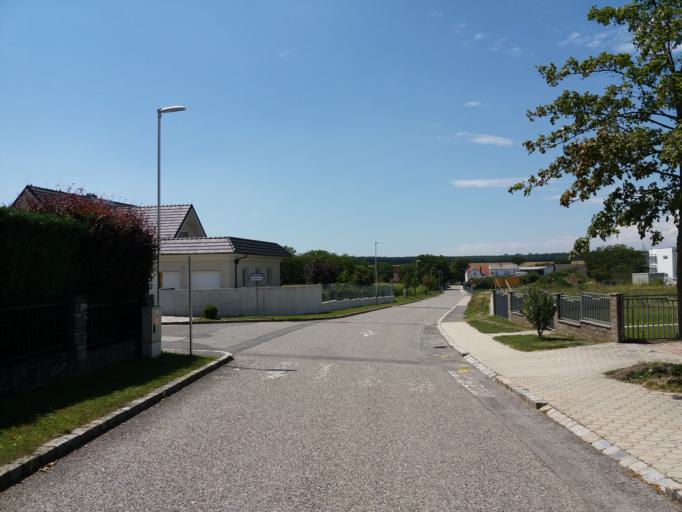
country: AT
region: Burgenland
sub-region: Politischer Bezirk Oberpullendorf
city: Raiding
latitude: 47.5665
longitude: 16.5346
